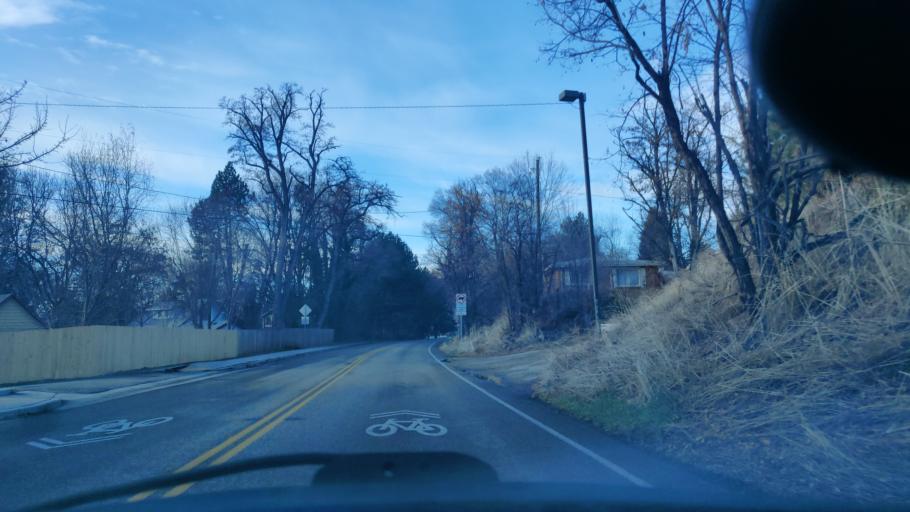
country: US
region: Idaho
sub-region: Ada County
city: Boise
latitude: 43.6369
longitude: -116.2037
